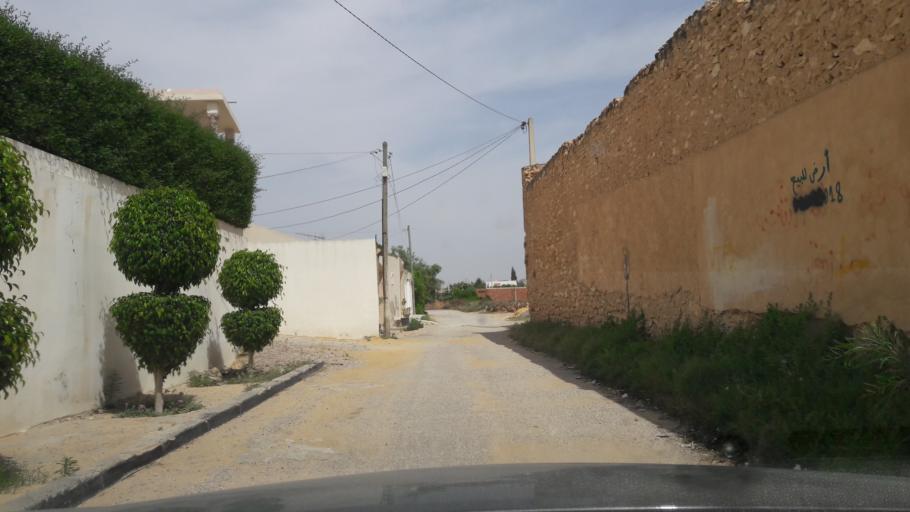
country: TN
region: Safaqis
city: Sfax
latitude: 34.7852
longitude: 10.7554
